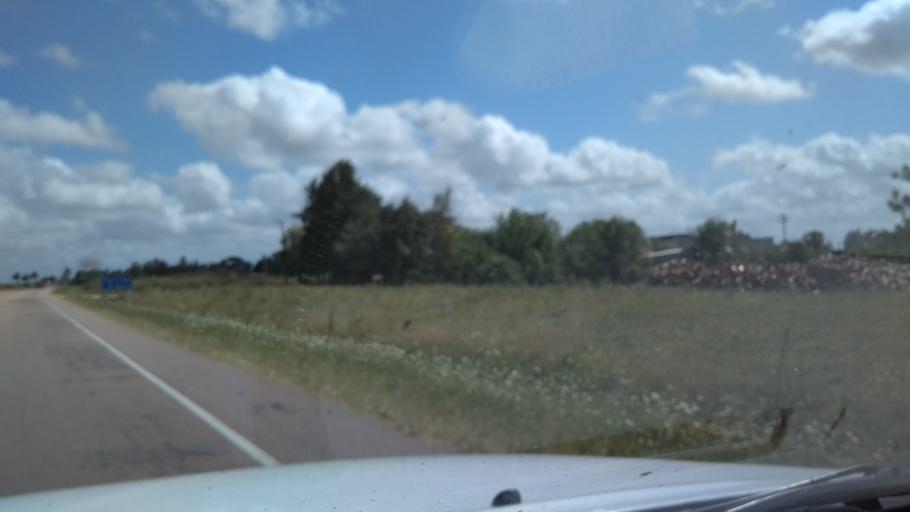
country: UY
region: Canelones
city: Sauce
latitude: -34.6588
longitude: -56.0559
